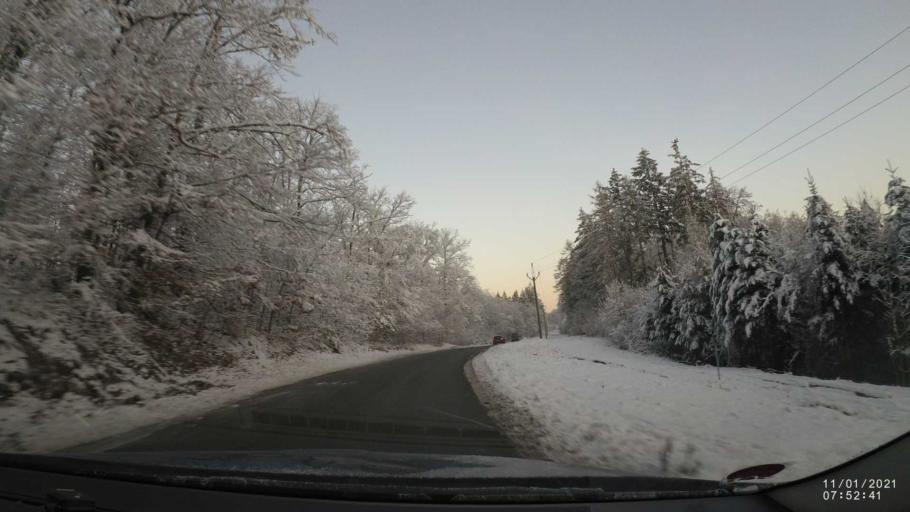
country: CZ
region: South Moravian
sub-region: Okres Blansko
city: Adamov
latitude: 49.2878
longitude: 16.6414
